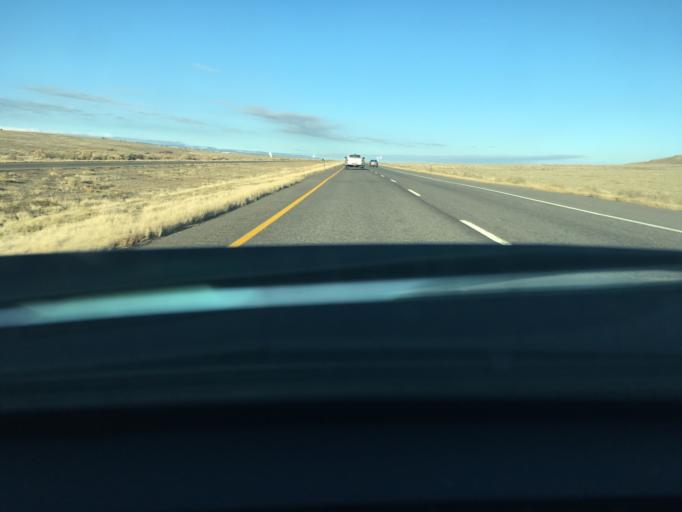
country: US
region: Colorado
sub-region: Delta County
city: Delta
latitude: 38.7778
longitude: -108.2336
